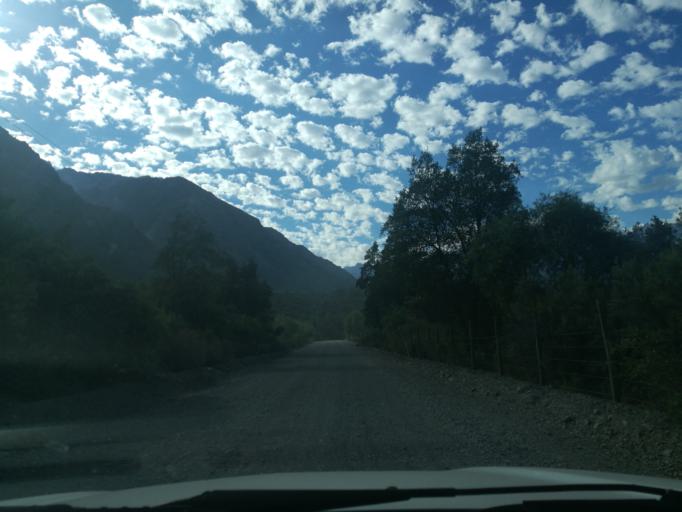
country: CL
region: O'Higgins
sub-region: Provincia de Cachapoal
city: Machali
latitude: -34.3010
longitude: -70.4247
